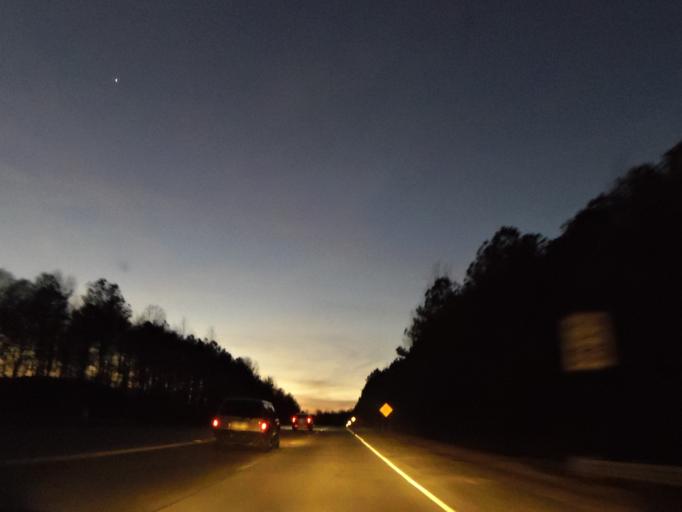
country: US
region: Georgia
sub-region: Whitfield County
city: Dalton
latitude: 34.8010
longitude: -84.9846
